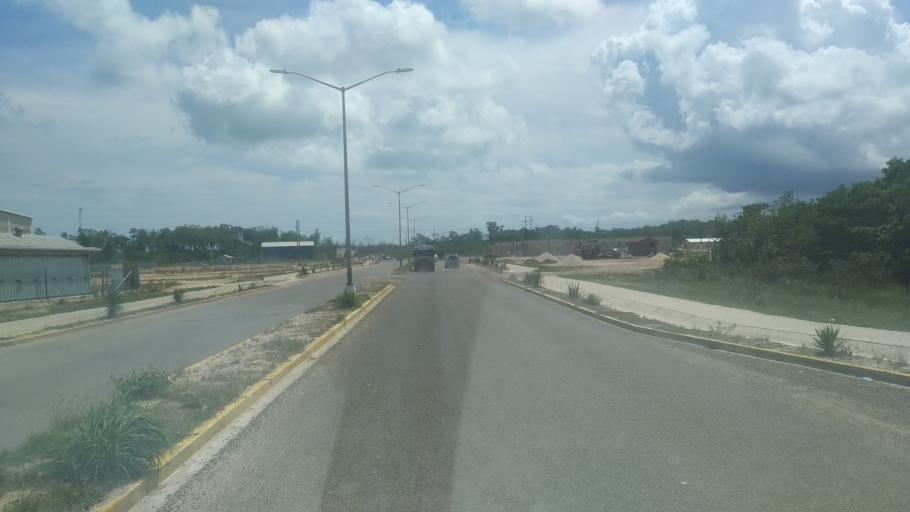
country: BZ
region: Belize
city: Belize City
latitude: 17.5059
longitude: -88.2217
